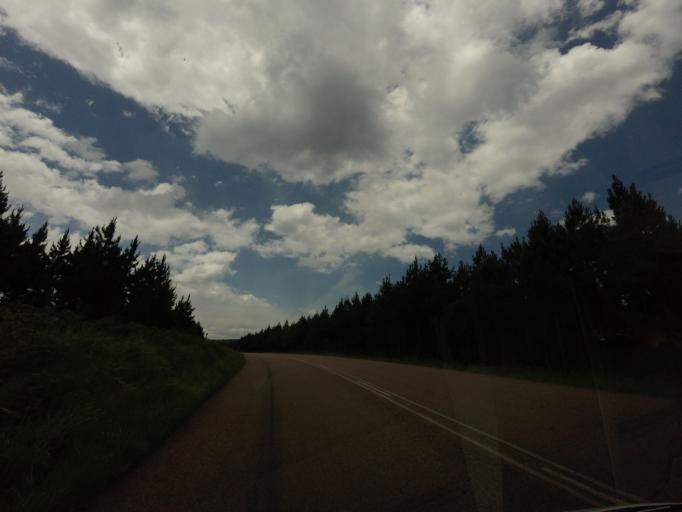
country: ZA
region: Mpumalanga
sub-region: Ehlanzeni District
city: Graksop
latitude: -25.0593
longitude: 30.8167
